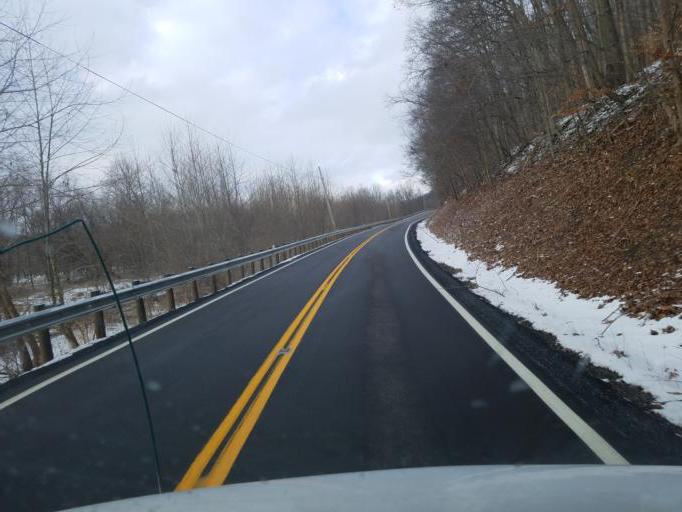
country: US
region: Ohio
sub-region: Holmes County
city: Millersburg
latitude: 40.4652
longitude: -81.9779
